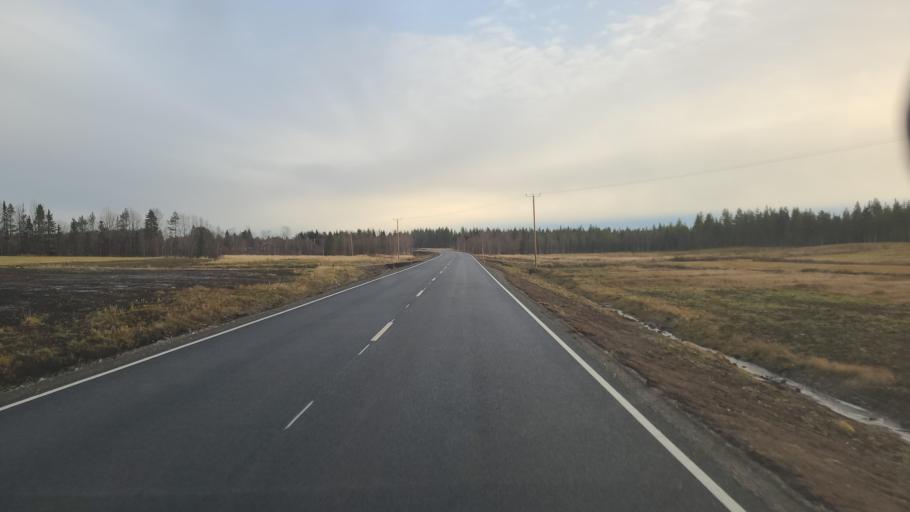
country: FI
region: Lapland
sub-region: Tunturi-Lappi
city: Kittilae
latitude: 67.8757
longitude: 24.8888
